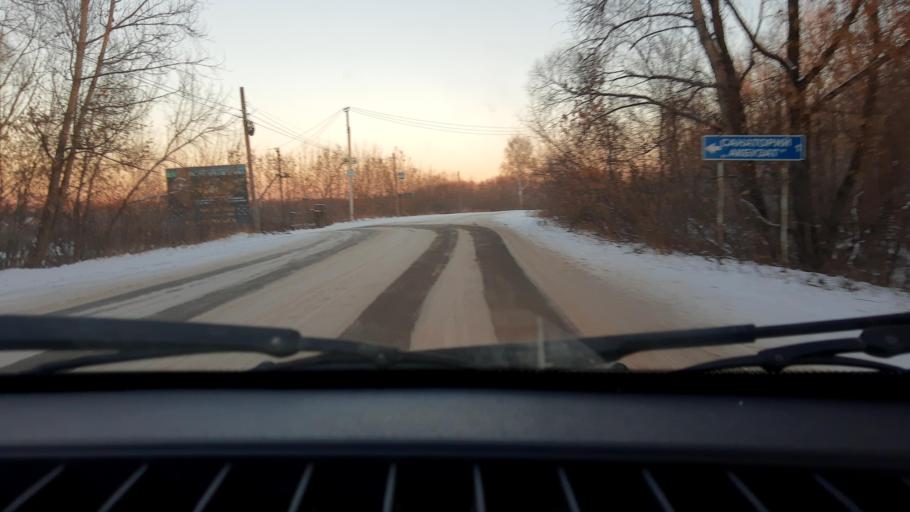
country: RU
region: Bashkortostan
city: Iglino
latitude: 54.8082
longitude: 56.1877
